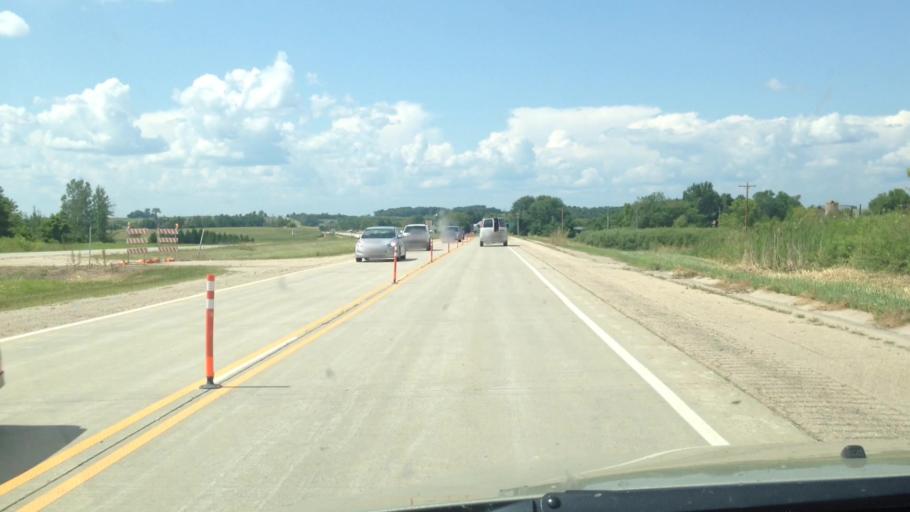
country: US
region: Wisconsin
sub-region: Shawano County
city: Bonduel
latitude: 44.7092
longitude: -88.3801
